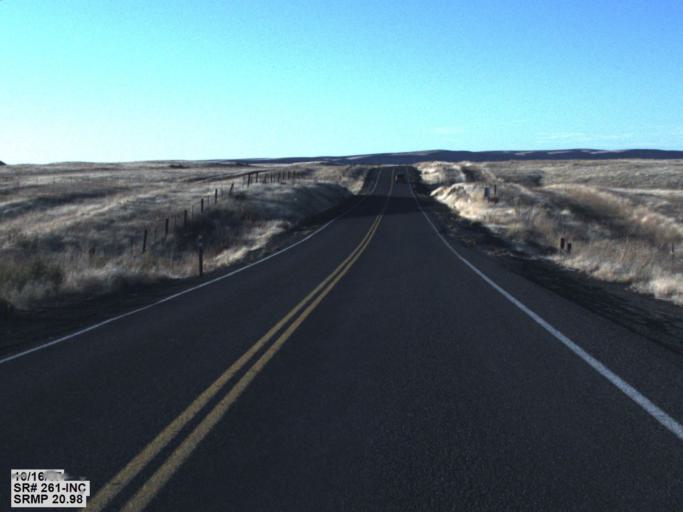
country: US
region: Washington
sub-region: Walla Walla County
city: Waitsburg
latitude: 46.6597
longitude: -118.2695
